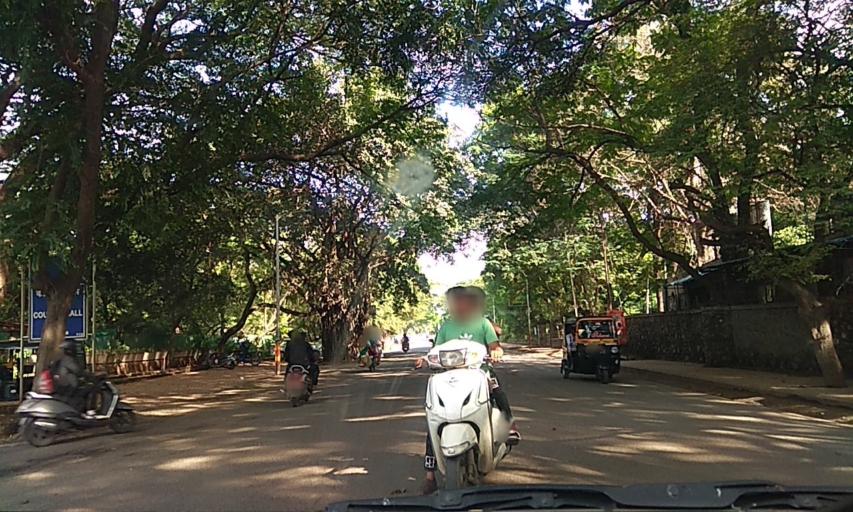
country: IN
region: Maharashtra
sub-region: Pune Division
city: Pune
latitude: 18.5243
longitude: 73.8802
